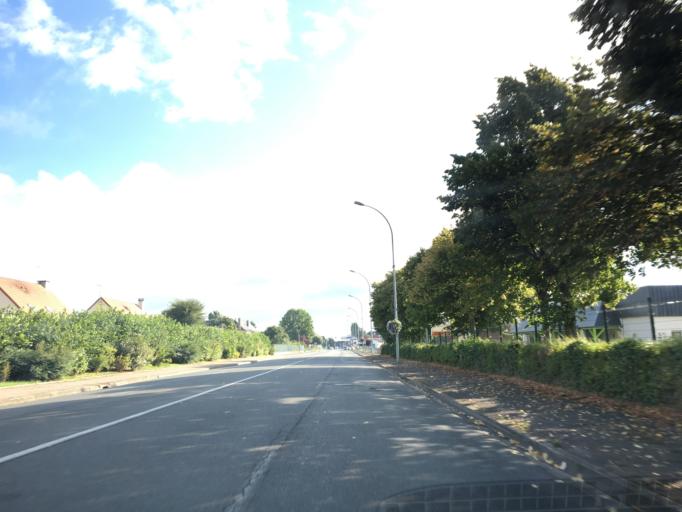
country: FR
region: Lower Normandy
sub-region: Departement du Calvados
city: Dives-sur-Mer
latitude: 49.2900
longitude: -0.0973
